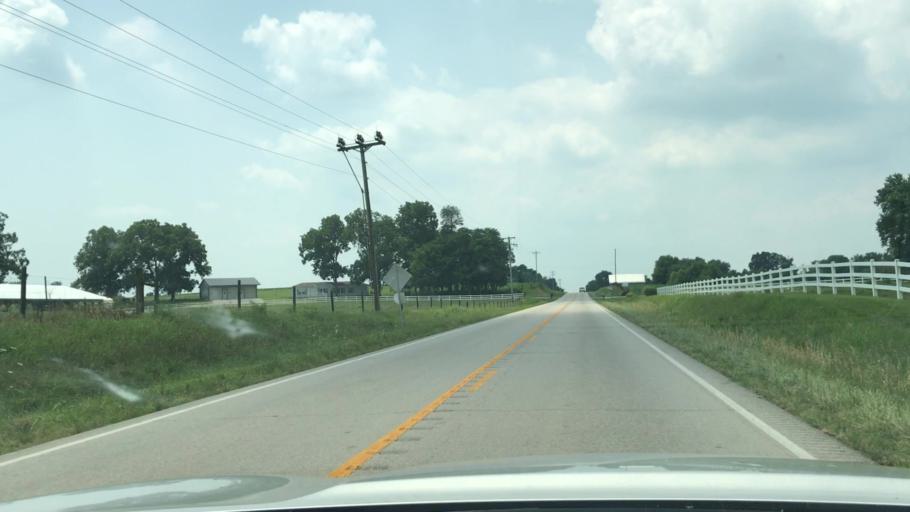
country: US
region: Kentucky
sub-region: Todd County
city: Guthrie
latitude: 36.6776
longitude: -87.1506
